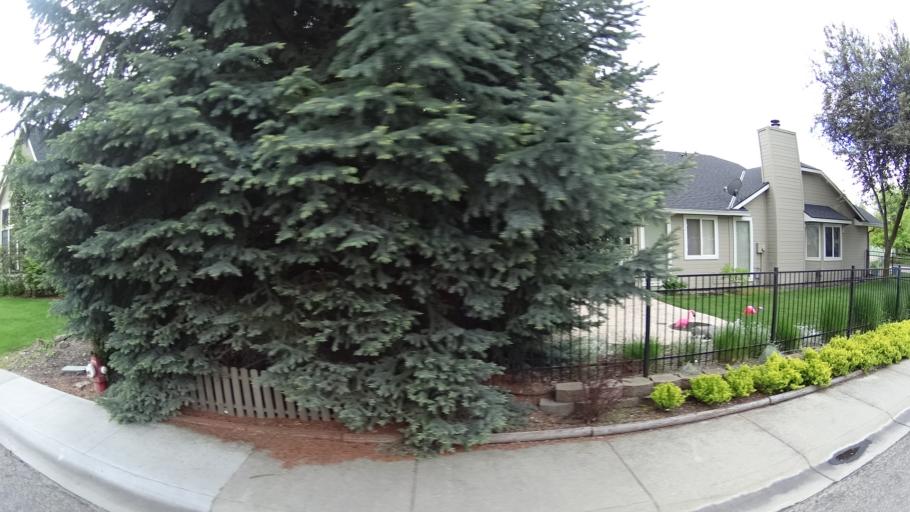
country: US
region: Idaho
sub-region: Ada County
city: Garden City
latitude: 43.6752
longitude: -116.2731
